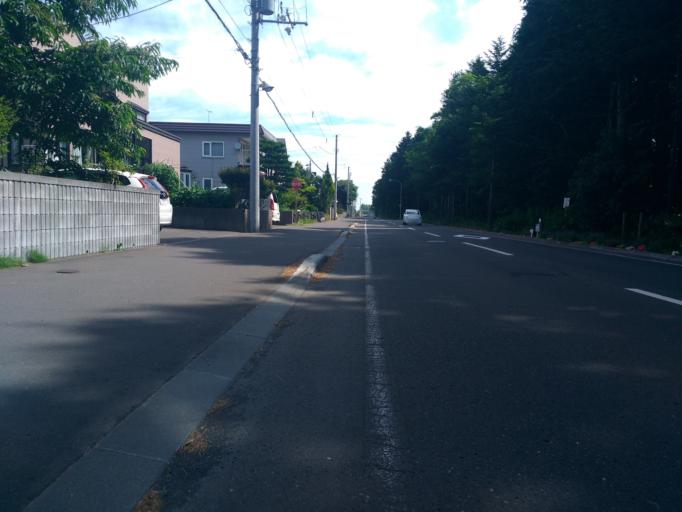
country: JP
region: Hokkaido
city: Ebetsu
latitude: 43.0784
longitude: 141.5078
